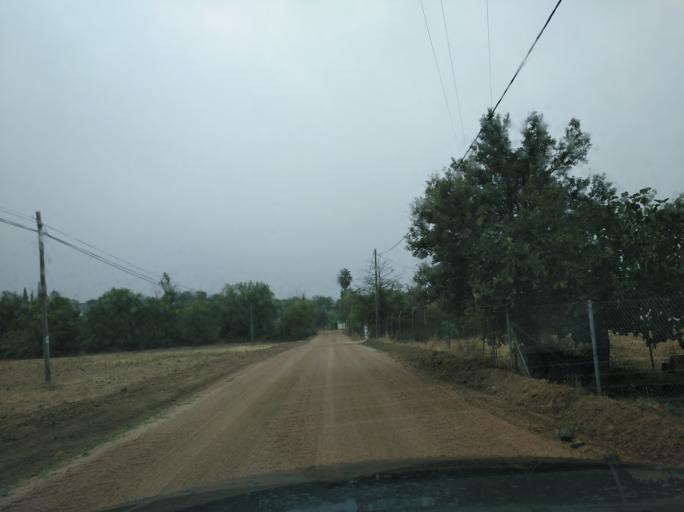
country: PT
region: Portalegre
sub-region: Campo Maior
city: Campo Maior
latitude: 38.9526
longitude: -7.0711
